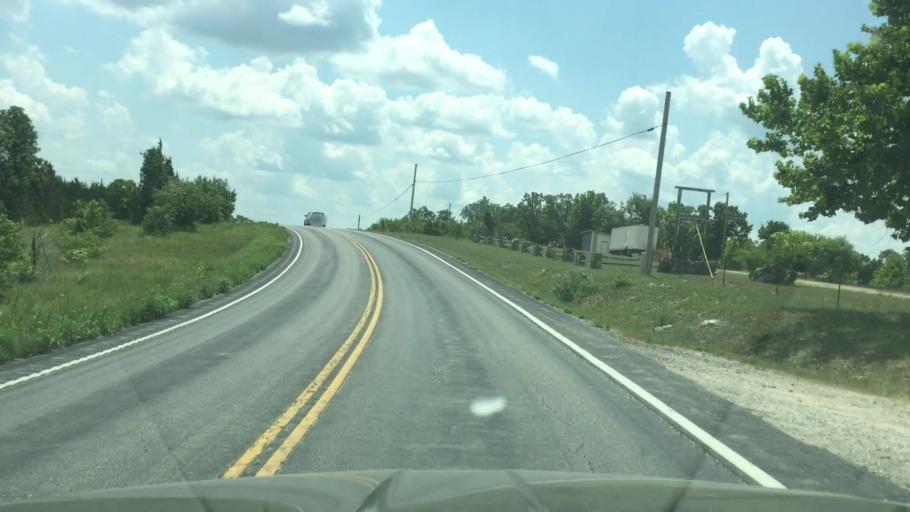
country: US
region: Missouri
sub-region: Miller County
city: Tuscumbia
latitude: 38.1062
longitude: -92.5010
